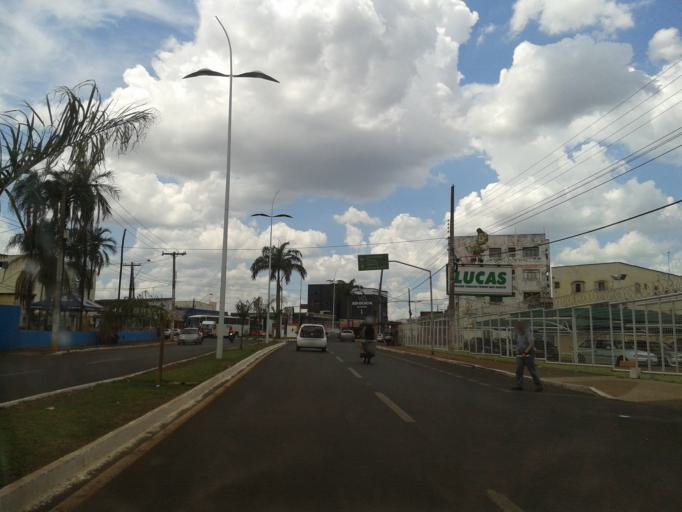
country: BR
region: Goias
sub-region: Itumbiara
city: Itumbiara
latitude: -18.4060
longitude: -49.2107
